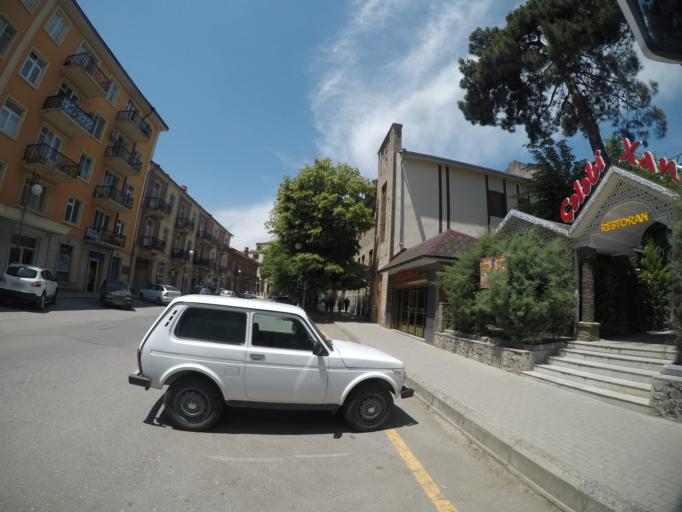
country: AZ
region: Shaki City
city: Sheki
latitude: 41.2029
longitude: 47.1796
